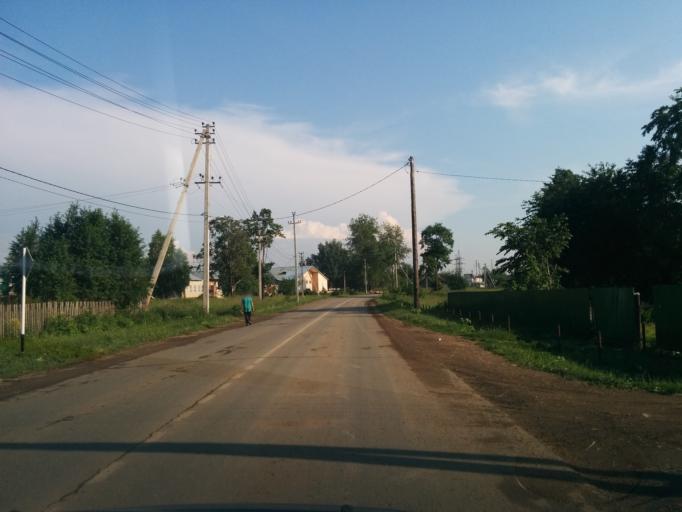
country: RU
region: Perm
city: Polazna
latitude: 58.2336
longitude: 56.2880
